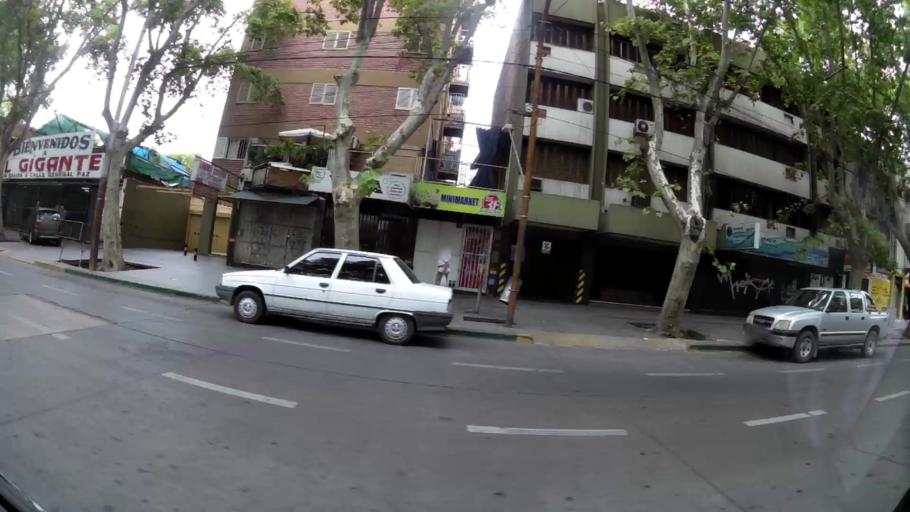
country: AR
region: Mendoza
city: Mendoza
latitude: -32.8835
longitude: -68.8413
